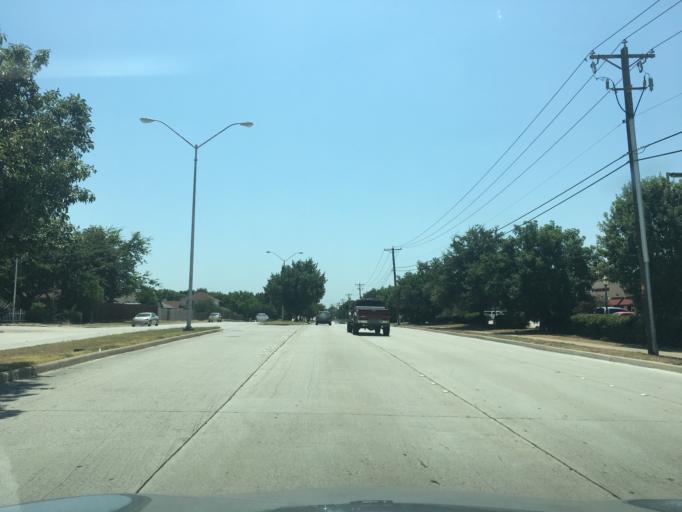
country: US
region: Texas
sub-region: Tarrant County
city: Edgecliff Village
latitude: 32.6326
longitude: -97.3699
